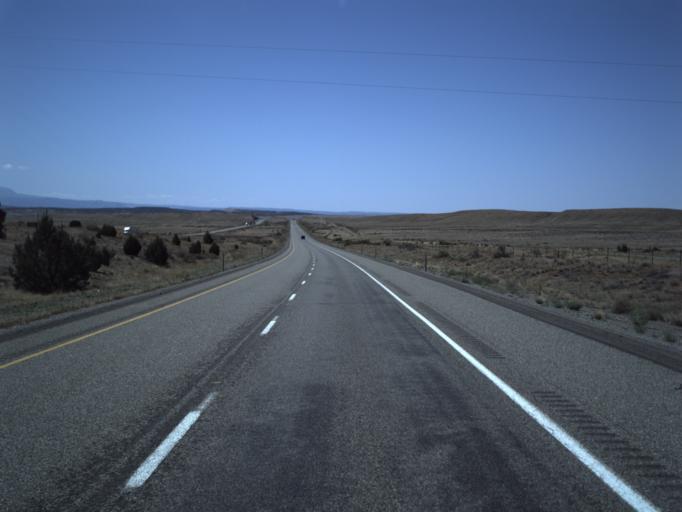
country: US
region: Colorado
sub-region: Mesa County
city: Loma
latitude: 39.1610
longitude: -109.1419
